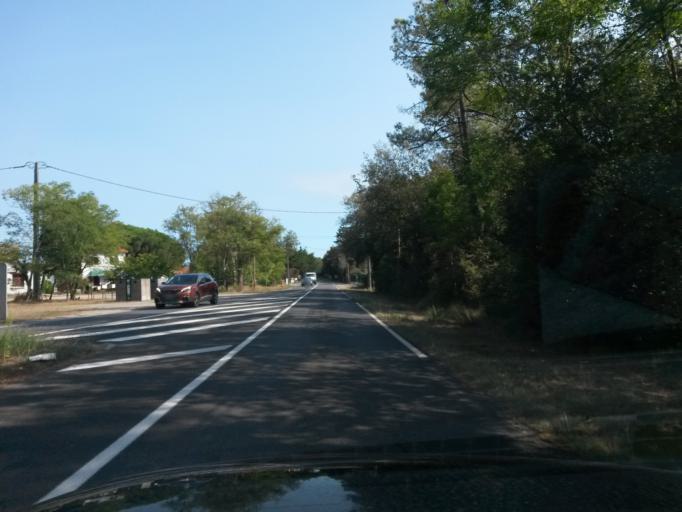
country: FR
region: Pays de la Loire
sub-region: Departement de la Vendee
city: Bretignolles-sur-Mer
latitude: 46.5844
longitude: -1.8272
